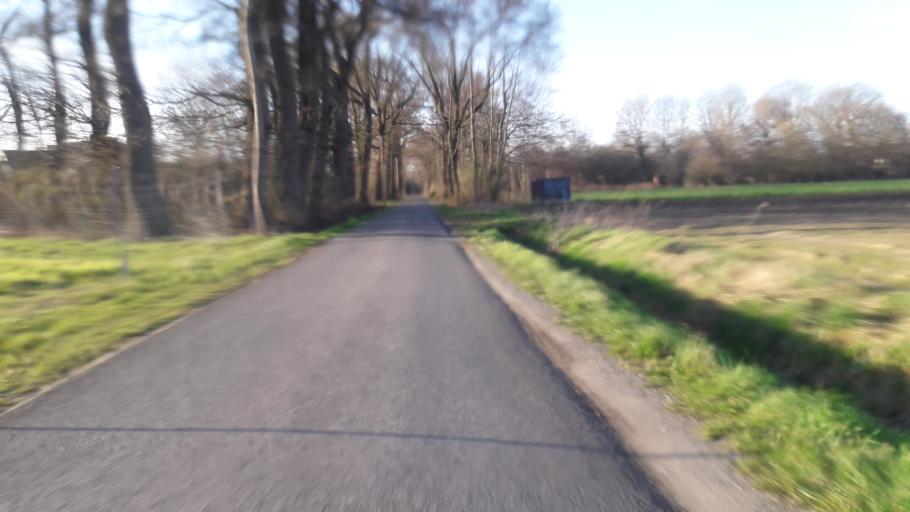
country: DE
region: North Rhine-Westphalia
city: Rietberg
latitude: 51.7850
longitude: 8.4661
